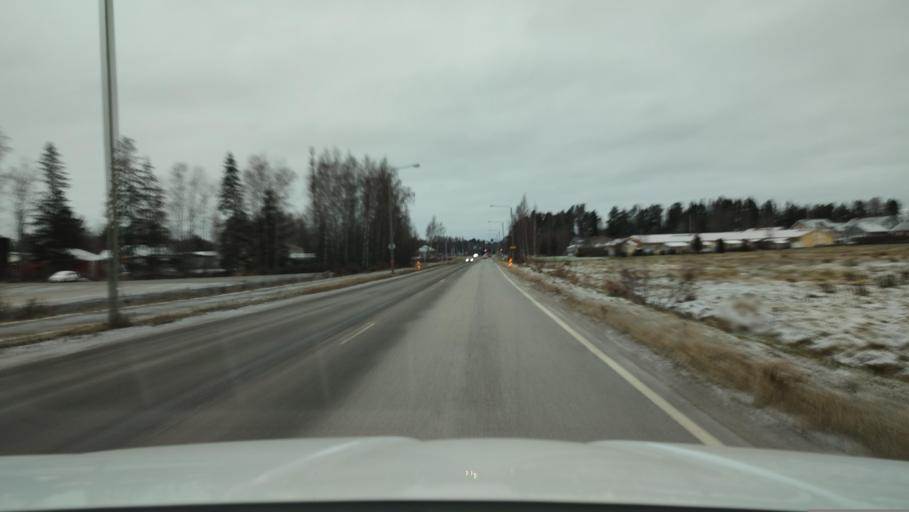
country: FI
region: Ostrobothnia
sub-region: Vaasa
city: Smedsby
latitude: 63.1176
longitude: 21.7133
